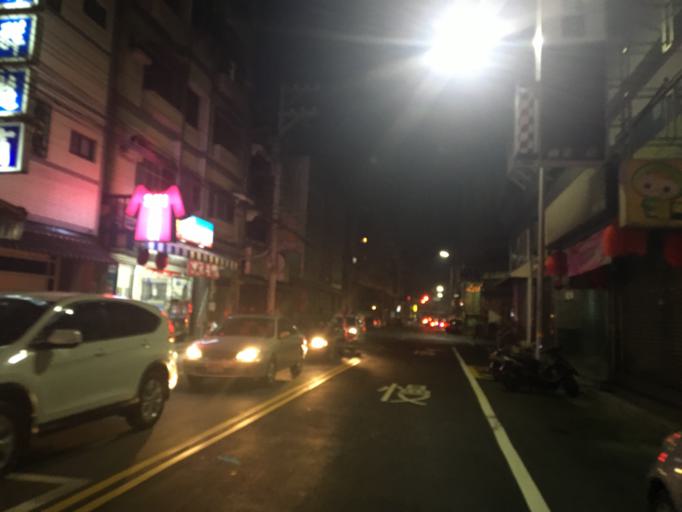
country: TW
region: Taiwan
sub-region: Hsinchu
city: Hsinchu
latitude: 24.8219
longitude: 120.9755
